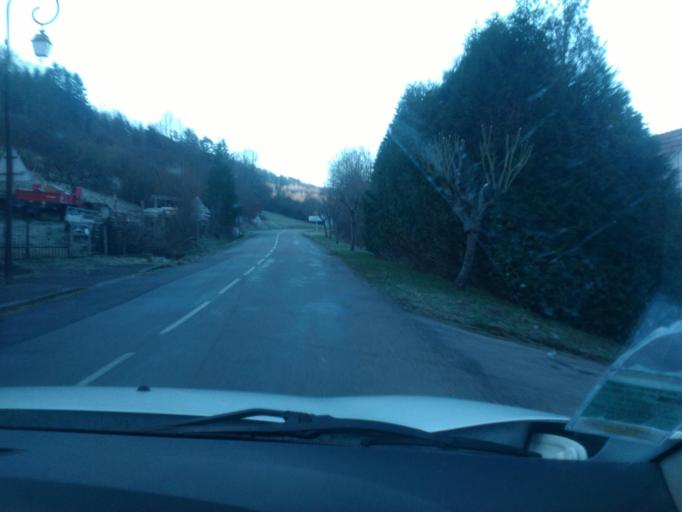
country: FR
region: Alsace
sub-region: Departement du Bas-Rhin
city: Russ
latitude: 48.4872
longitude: 7.2444
